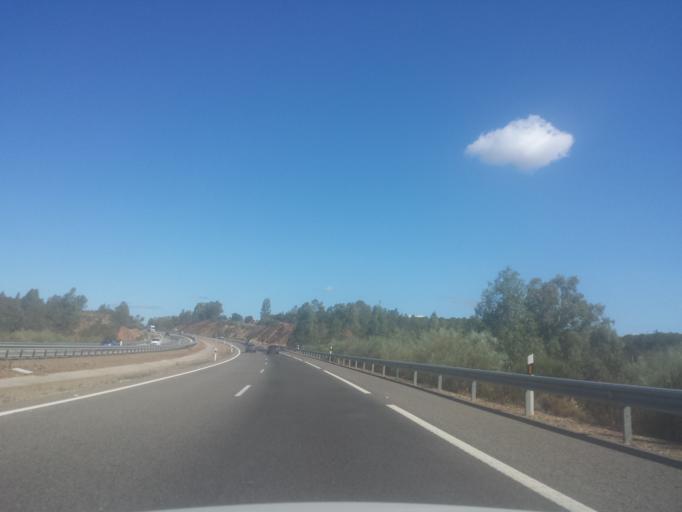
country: ES
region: Andalusia
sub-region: Provincia de Huelva
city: Santa Olalla del Cala
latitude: 37.8113
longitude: -6.2042
